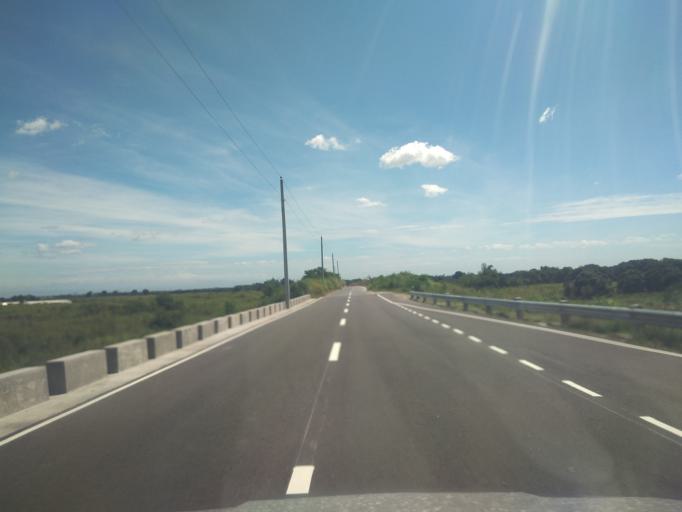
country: PH
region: Central Luzon
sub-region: Province of Pampanga
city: Balas
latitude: 15.0547
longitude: 120.5743
